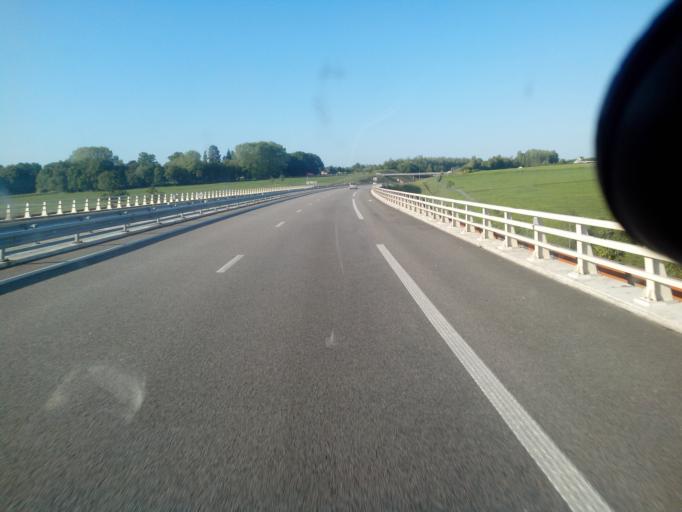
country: FR
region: Haute-Normandie
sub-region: Departement de la Seine-Maritime
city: Nointot
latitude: 49.5960
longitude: 0.4538
